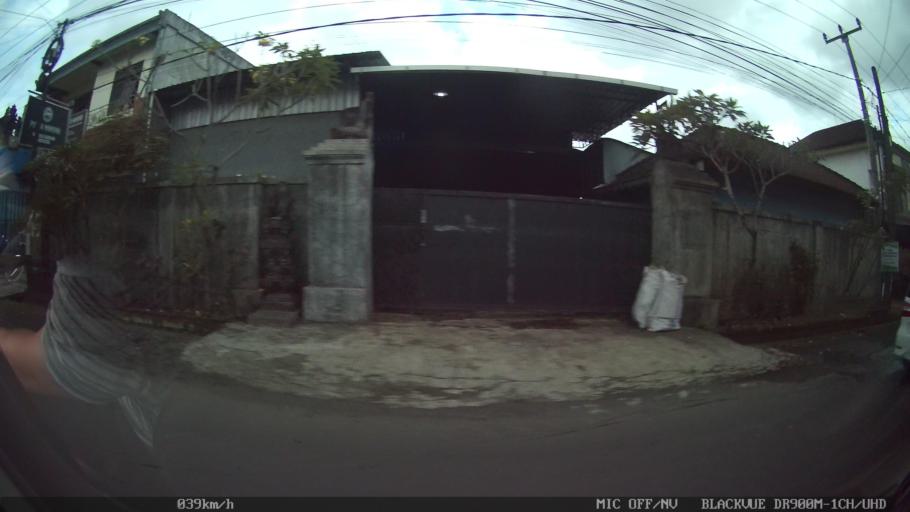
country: ID
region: Bali
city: Banjar Tegal Belodan
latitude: -8.5464
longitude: 115.1202
